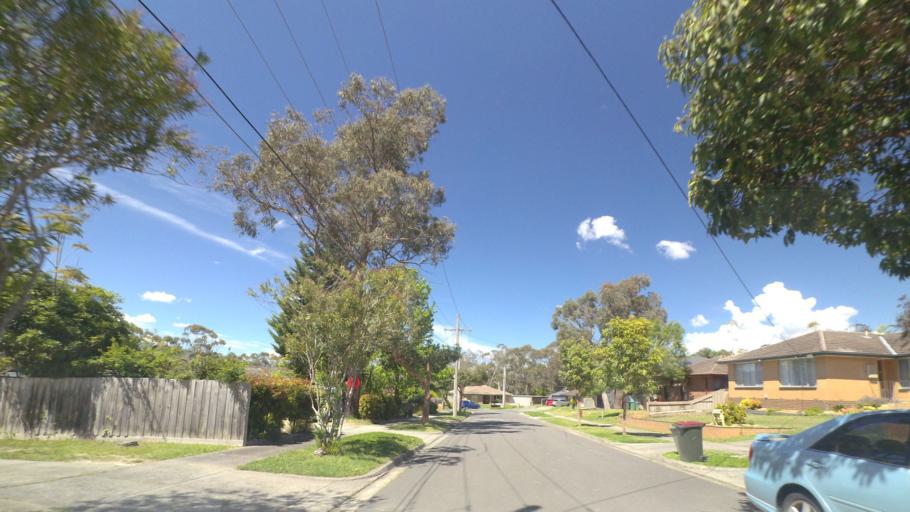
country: AU
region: Victoria
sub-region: Maroondah
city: Croydon South
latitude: -37.8208
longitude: 145.2779
